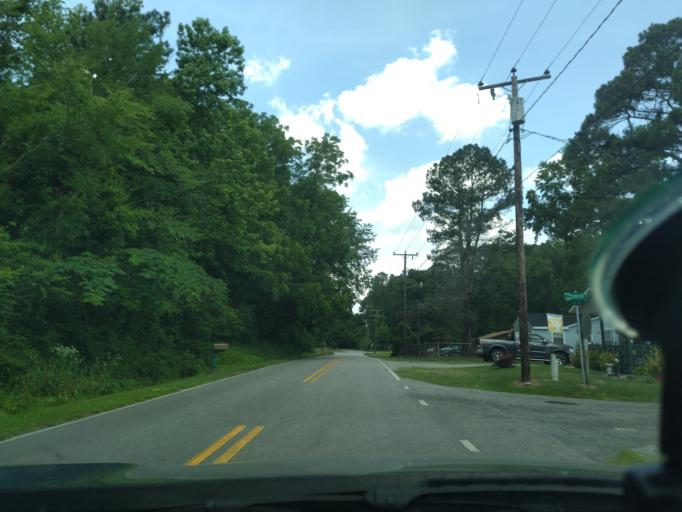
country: US
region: North Carolina
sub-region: Washington County
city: Plymouth
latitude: 35.8488
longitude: -76.7707
